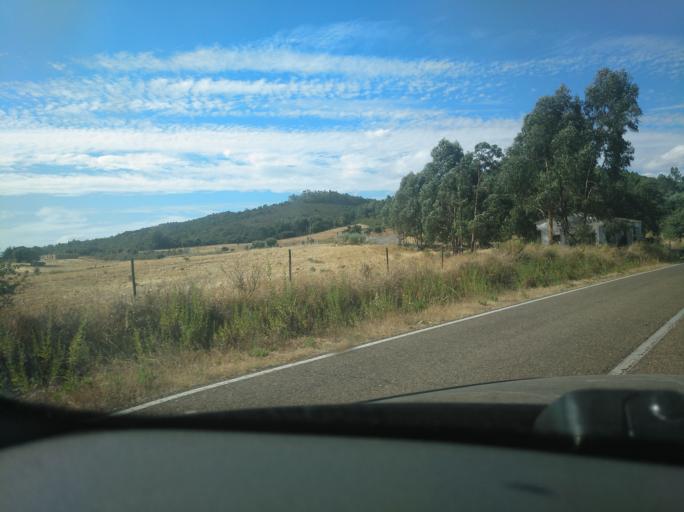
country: ES
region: Extremadura
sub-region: Provincia de Badajoz
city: La Codosera
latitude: 39.1838
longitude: -7.1758
